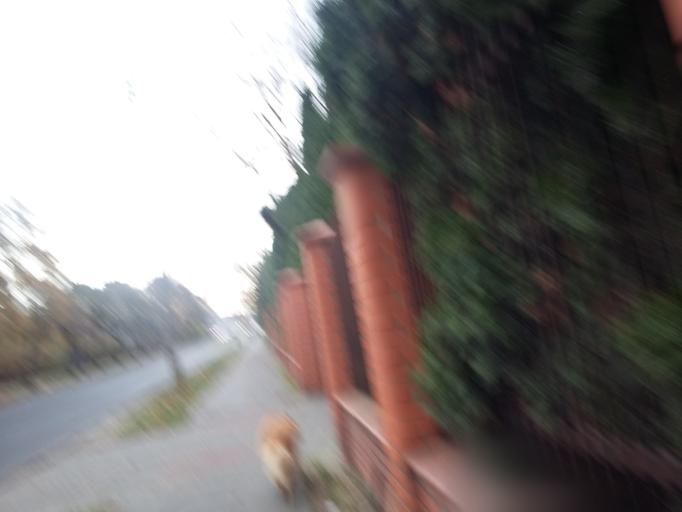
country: PL
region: Lodz Voivodeship
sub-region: Powiat pabianicki
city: Ksawerow
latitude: 51.7126
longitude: 19.4250
